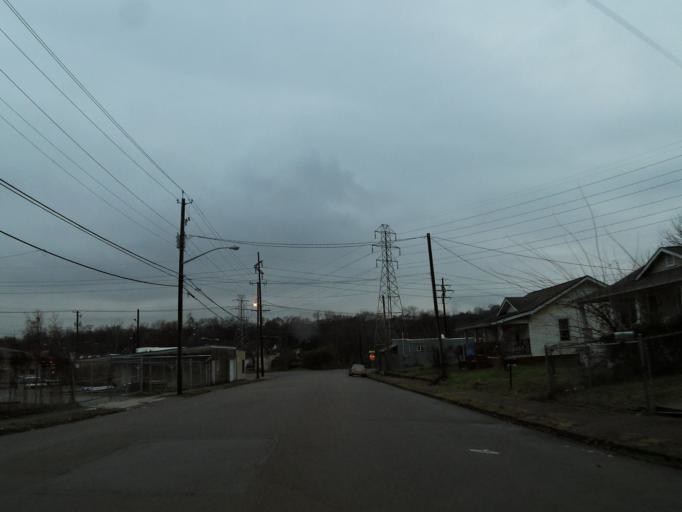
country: US
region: Tennessee
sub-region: Knox County
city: Knoxville
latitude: 35.9899
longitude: -83.9146
